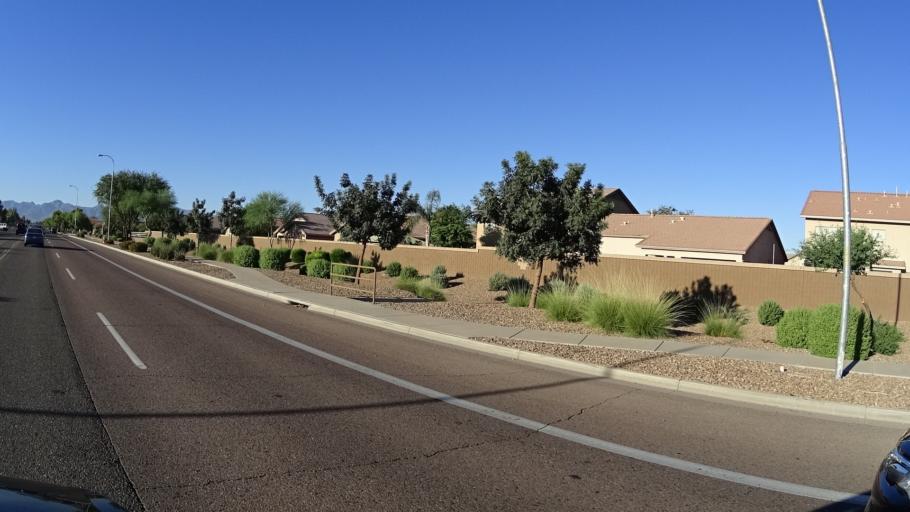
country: US
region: Arizona
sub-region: Maricopa County
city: Tolleson
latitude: 33.4314
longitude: -112.2385
